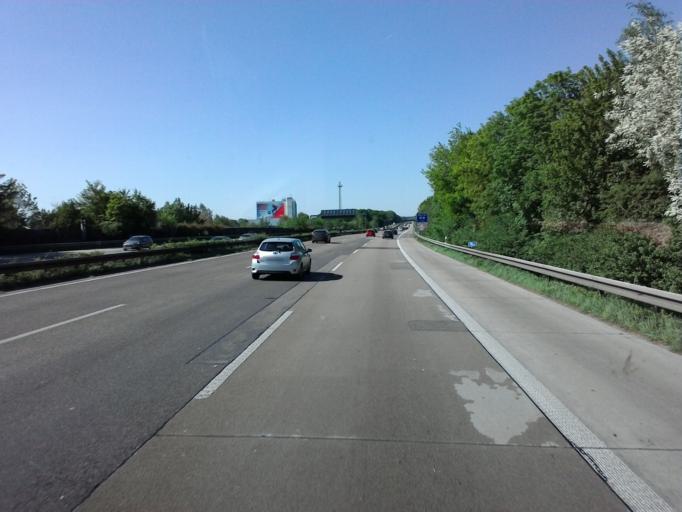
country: DE
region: North Rhine-Westphalia
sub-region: Regierungsbezirk Dusseldorf
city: Langenfeld
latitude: 51.1275
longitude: 6.9758
